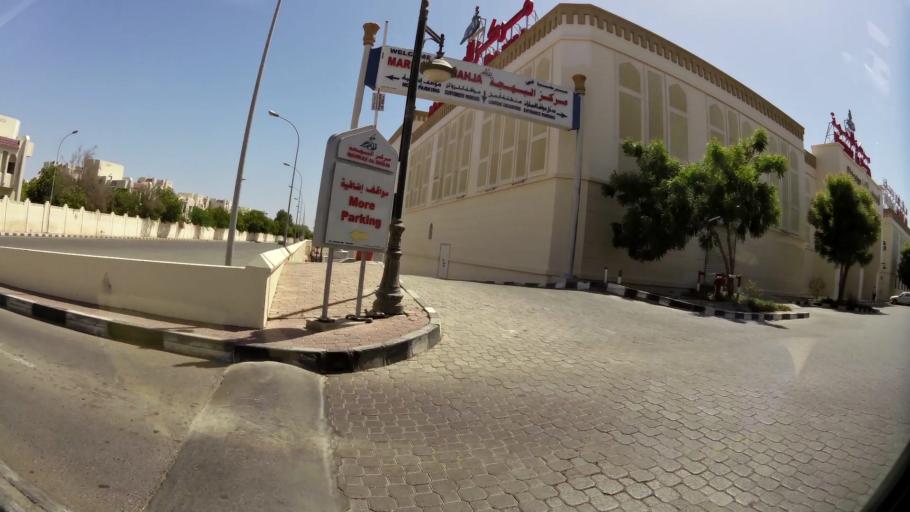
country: OM
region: Muhafazat Masqat
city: As Sib al Jadidah
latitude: 23.6139
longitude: 58.2458
